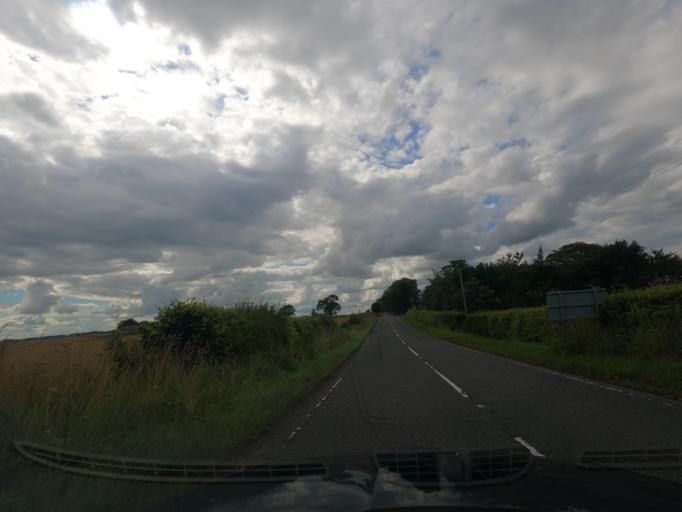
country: GB
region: Scotland
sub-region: The Scottish Borders
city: Kelso
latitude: 55.7030
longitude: -2.4241
